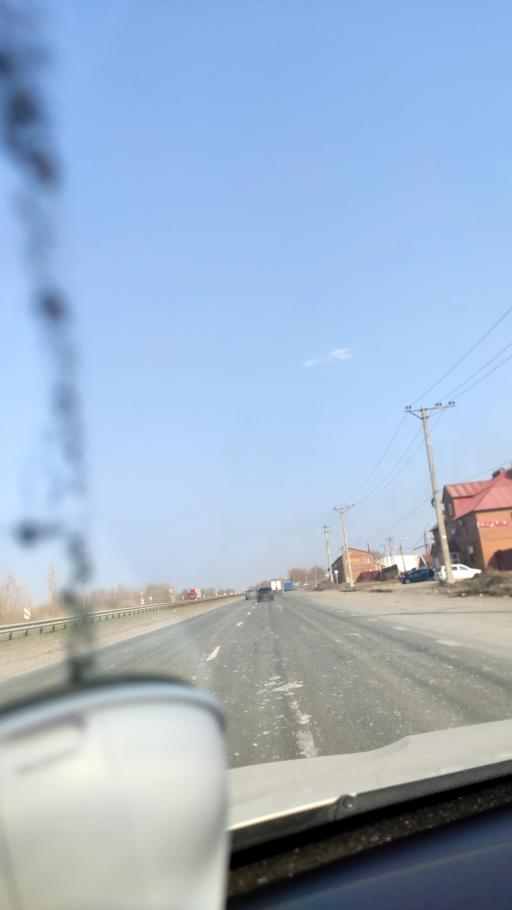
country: RU
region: Samara
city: Smyshlyayevka
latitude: 53.2582
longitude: 50.4367
